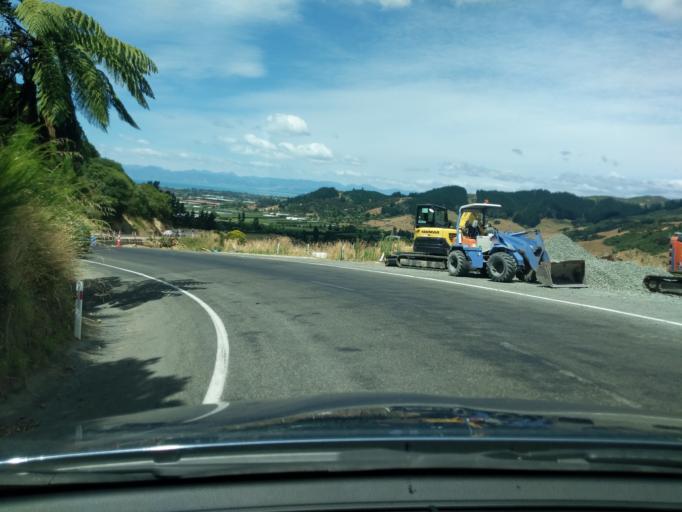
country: NZ
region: Tasman
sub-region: Tasman District
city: Motueka
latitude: -41.0482
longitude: 172.9579
